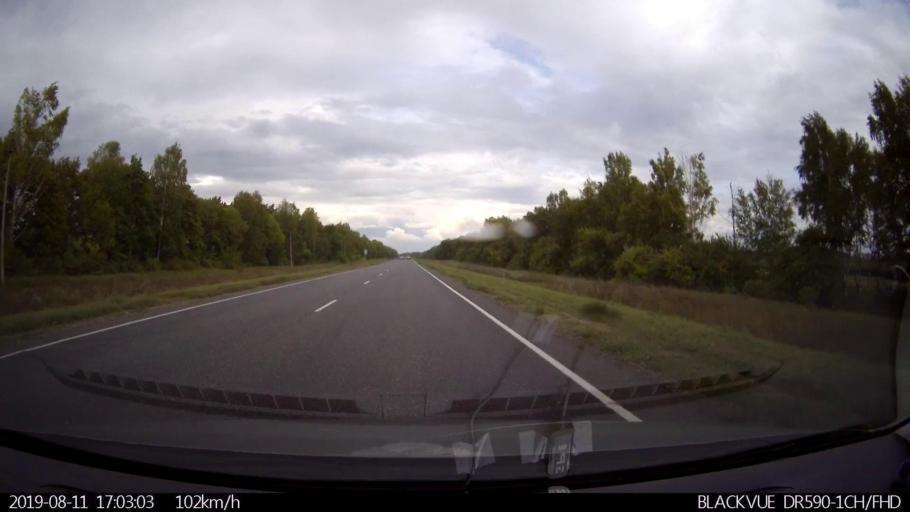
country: RU
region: Ulyanovsk
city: Mayna
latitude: 54.3042
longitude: 47.7298
